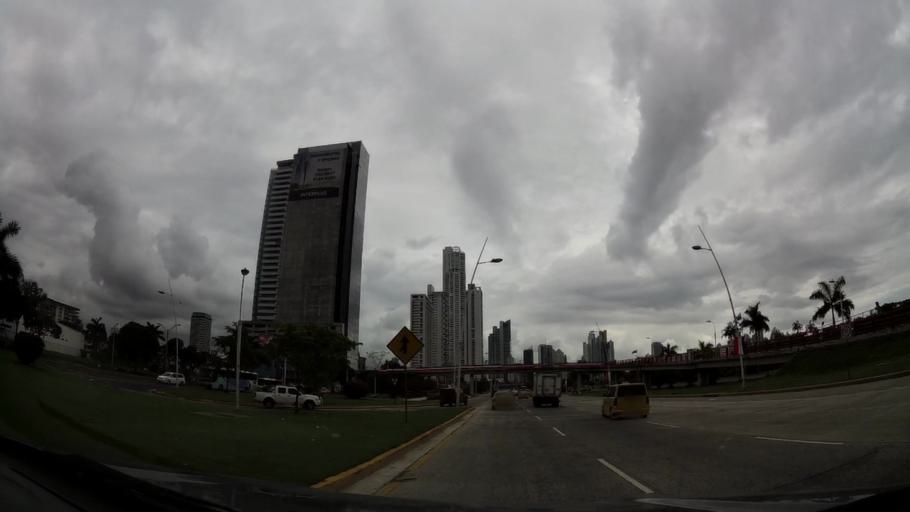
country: PA
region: Panama
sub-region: Distrito de Panama
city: Ancon
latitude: 8.9617
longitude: -79.5360
